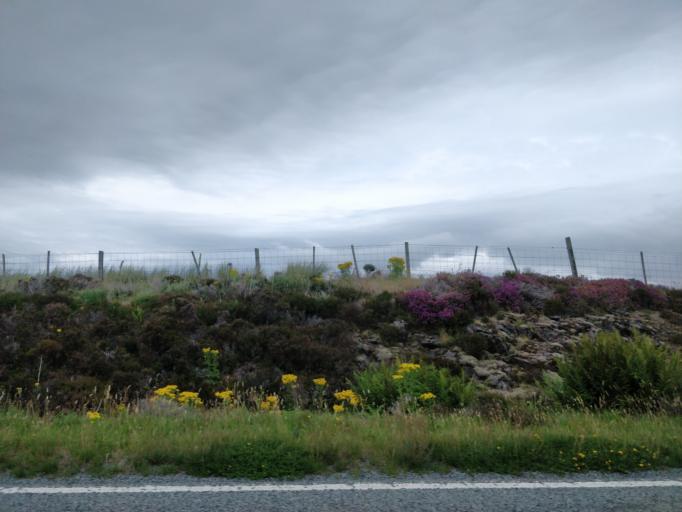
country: GB
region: Scotland
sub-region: Highland
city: Isle of Skye
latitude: 57.3705
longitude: -6.4530
